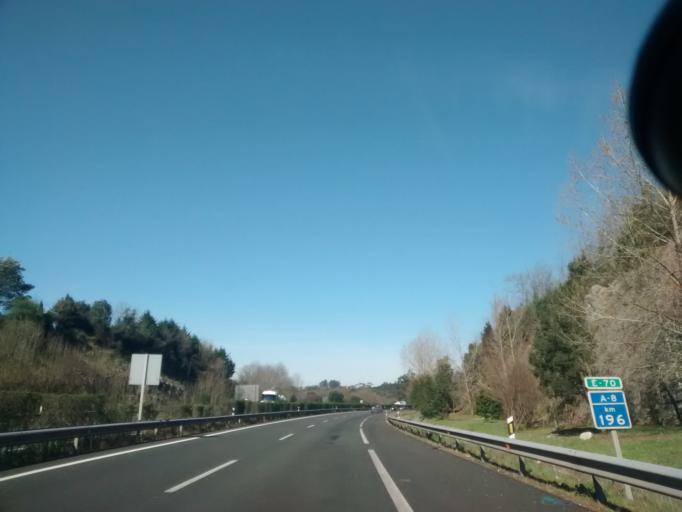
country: ES
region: Cantabria
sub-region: Provincia de Cantabria
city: Entrambasaguas
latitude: 43.3907
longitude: -3.6925
